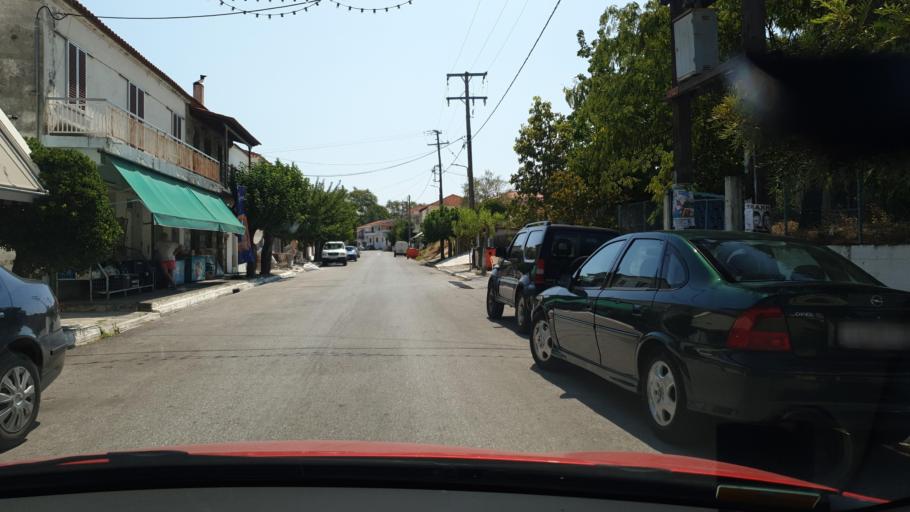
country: GR
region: Central Greece
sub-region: Nomos Evvoias
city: Oxilithos
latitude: 38.5440
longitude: 24.0748
